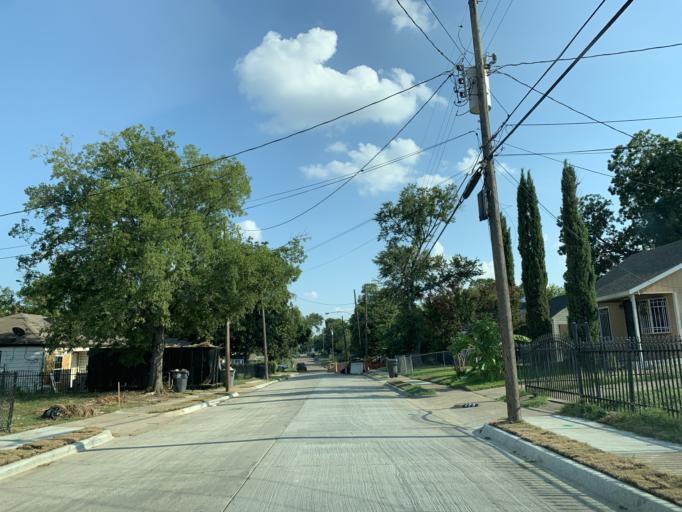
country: US
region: Texas
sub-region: Dallas County
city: Dallas
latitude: 32.7440
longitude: -96.7927
